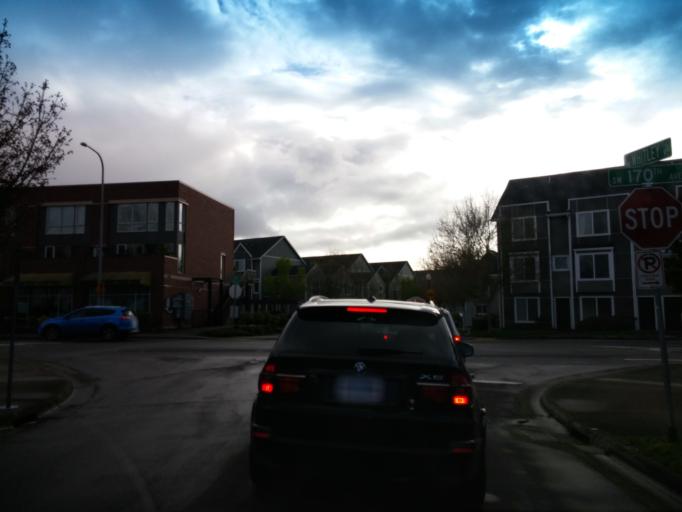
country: US
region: Oregon
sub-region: Washington County
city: Aloha
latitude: 45.5136
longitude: -122.8521
